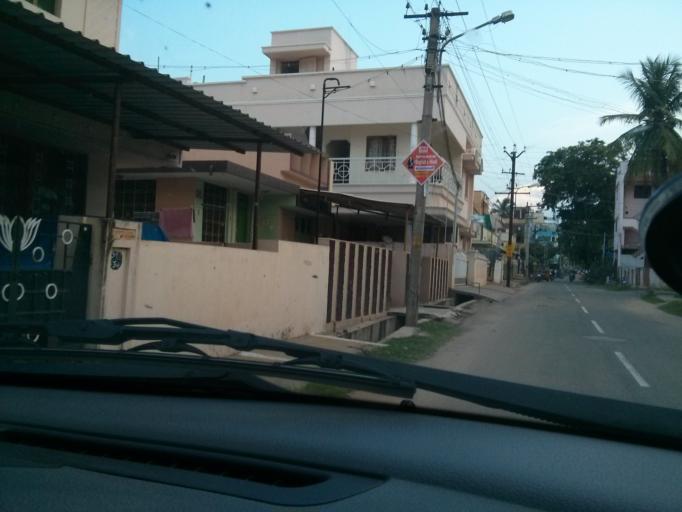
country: IN
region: Tamil Nadu
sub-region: Coimbatore
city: Coimbatore
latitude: 11.0322
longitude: 76.9426
